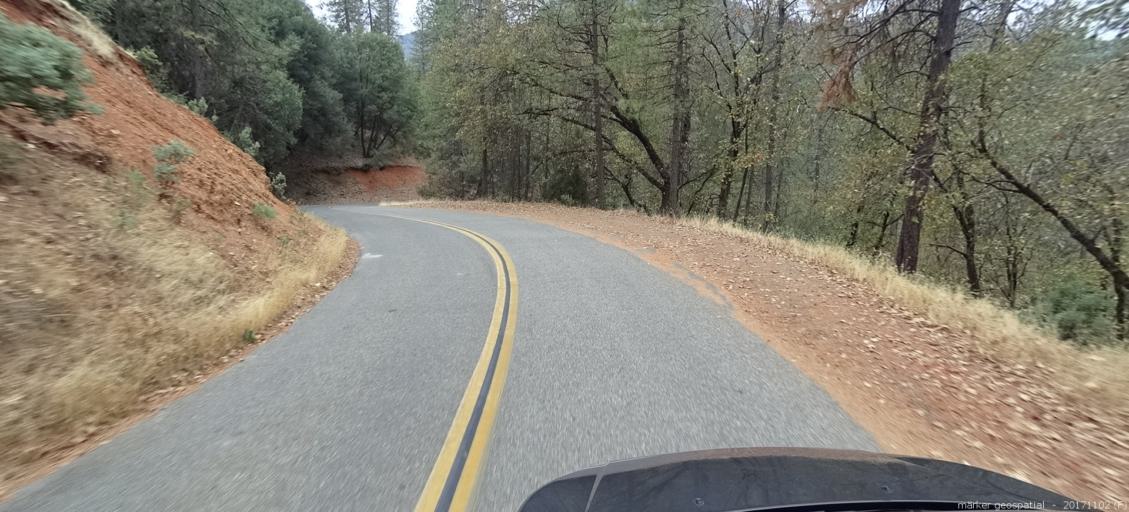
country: US
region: California
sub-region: Shasta County
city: Bella Vista
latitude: 40.7366
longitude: -122.2388
